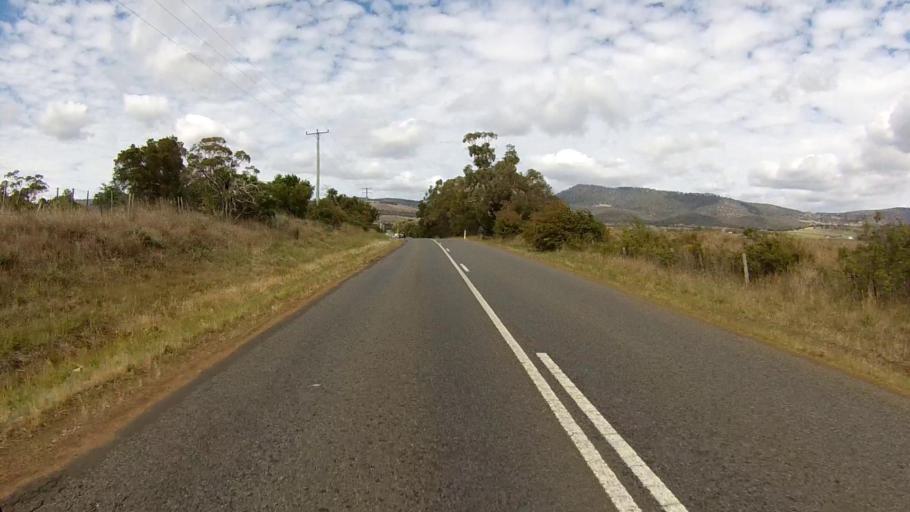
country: AU
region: Tasmania
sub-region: Clarence
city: Cambridge
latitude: -42.7473
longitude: 147.4146
